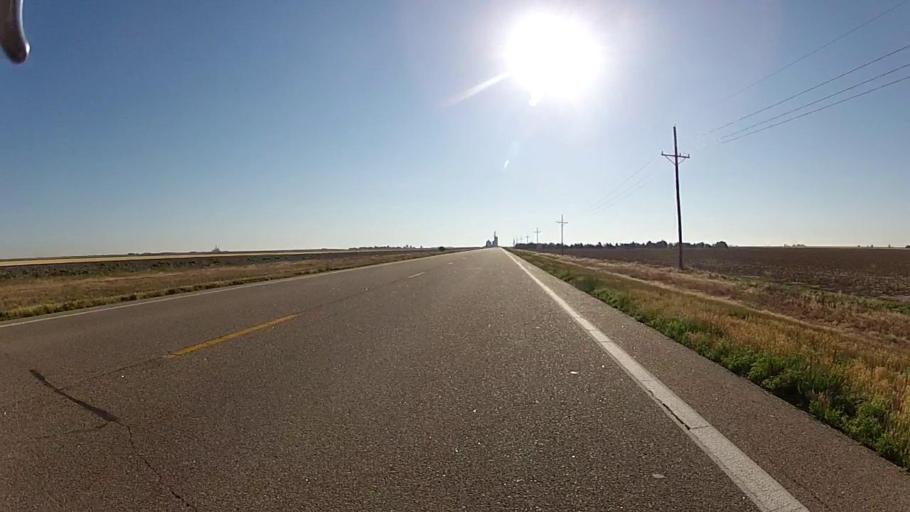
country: US
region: Kansas
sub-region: Haskell County
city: Sublette
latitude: 37.5120
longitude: -100.7410
